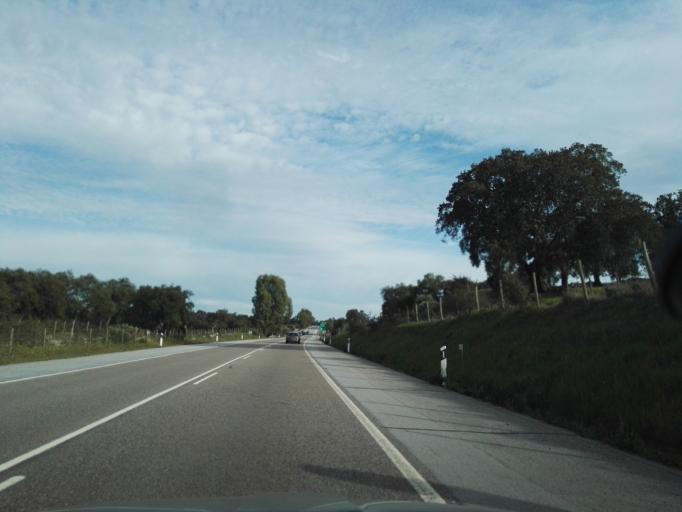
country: PT
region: Portalegre
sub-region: Nisa
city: Nisa
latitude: 39.4300
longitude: -7.7158
